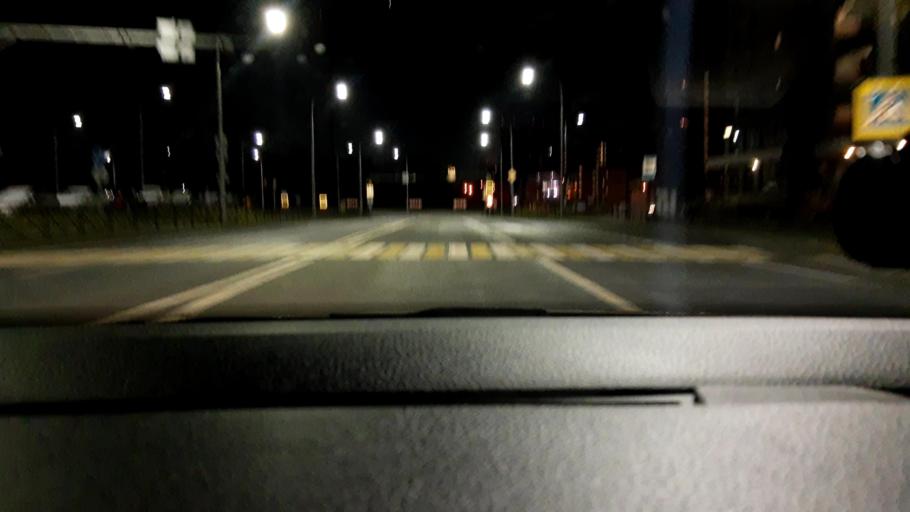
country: RU
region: Moskovskaya
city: Mytishchi
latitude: 55.9228
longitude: 37.7269
